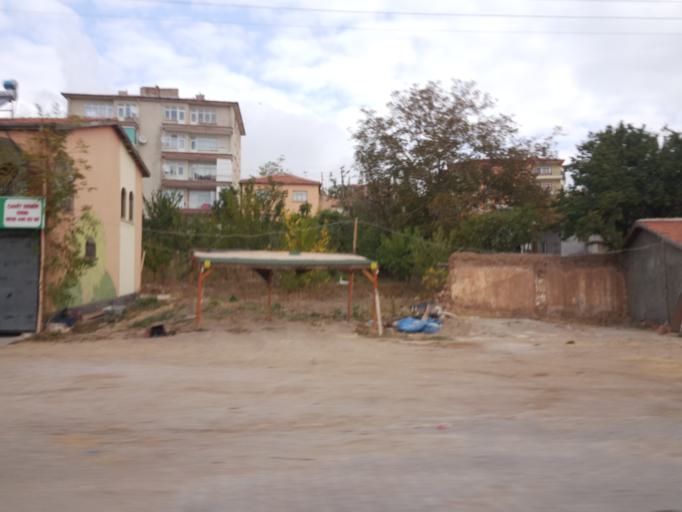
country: TR
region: Kirikkale
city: Keskin
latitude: 39.6733
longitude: 33.6060
